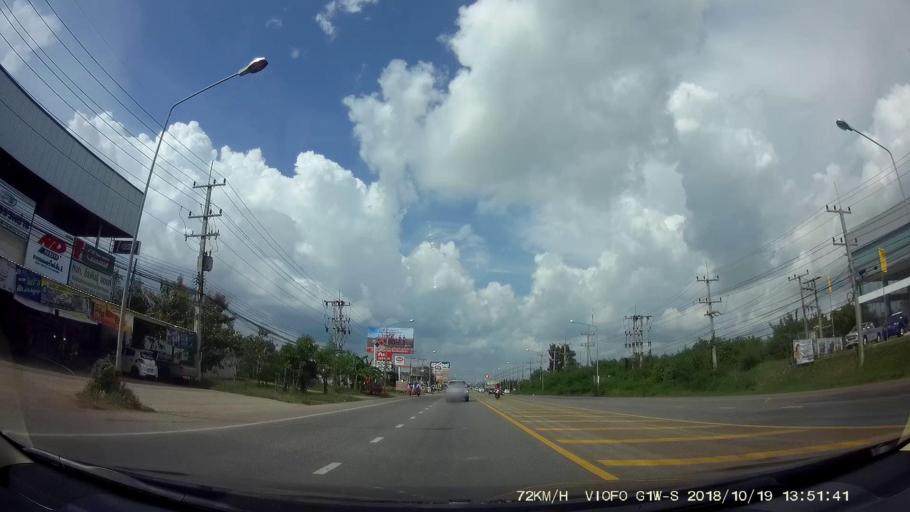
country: TH
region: Chaiyaphum
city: Chaiyaphum
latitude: 15.7592
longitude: 102.0244
